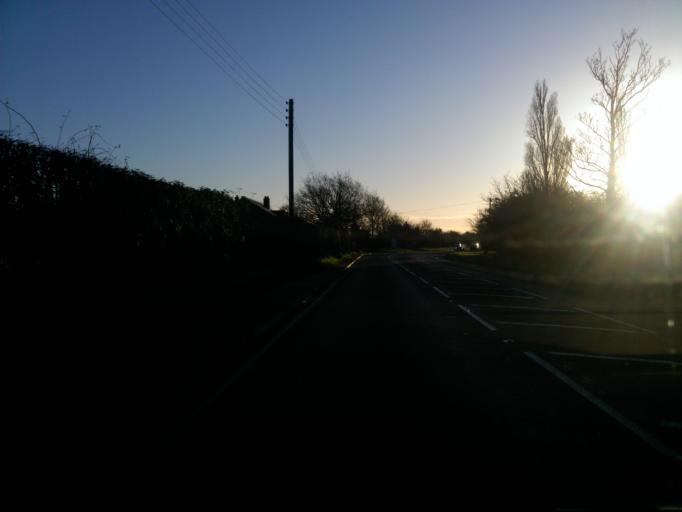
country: GB
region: England
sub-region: Essex
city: Alresford
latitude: 51.8561
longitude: 1.0016
